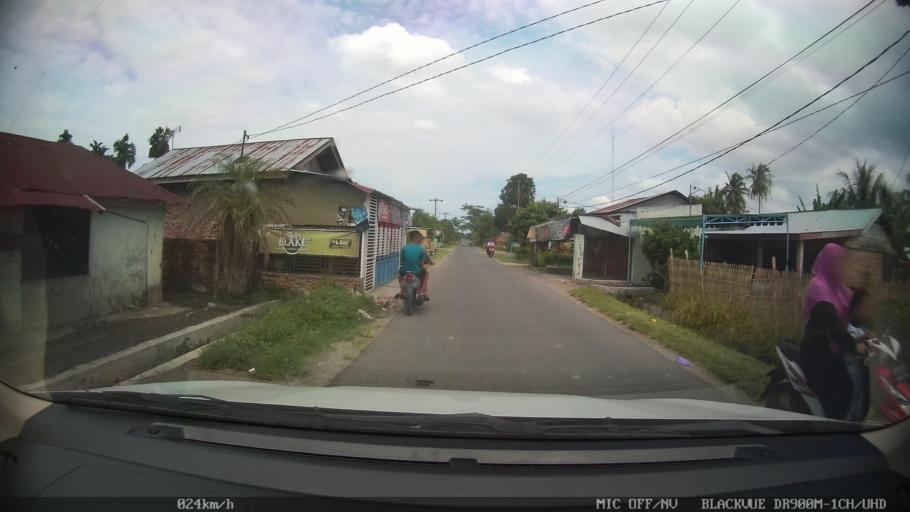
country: ID
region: North Sumatra
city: Sunggal
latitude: 3.6359
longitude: 98.5946
